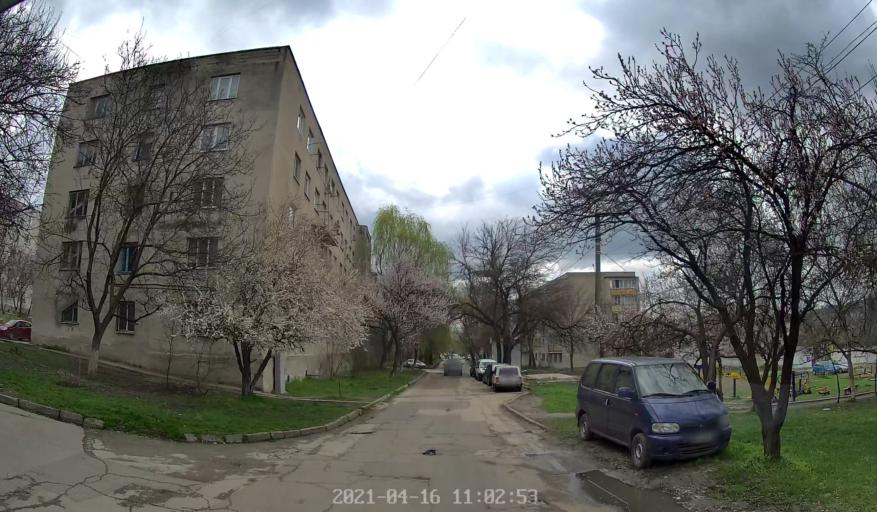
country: MD
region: Chisinau
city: Stauceni
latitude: 47.0643
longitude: 28.8479
